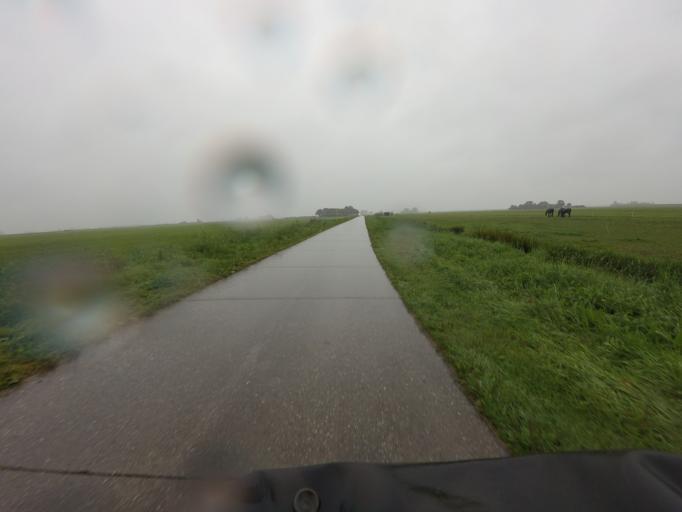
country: NL
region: Friesland
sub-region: Sudwest Fryslan
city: Bolsward
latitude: 53.0145
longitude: 5.5197
